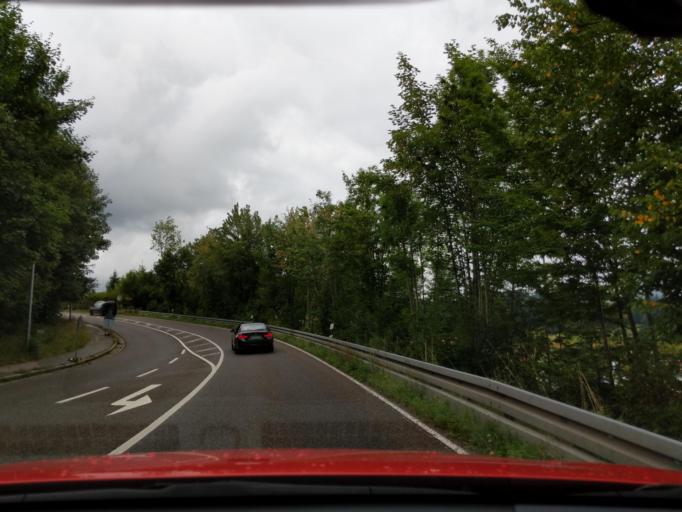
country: DE
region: Bavaria
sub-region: Swabia
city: Immenstadt im Allgau
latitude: 47.5677
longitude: 10.1926
